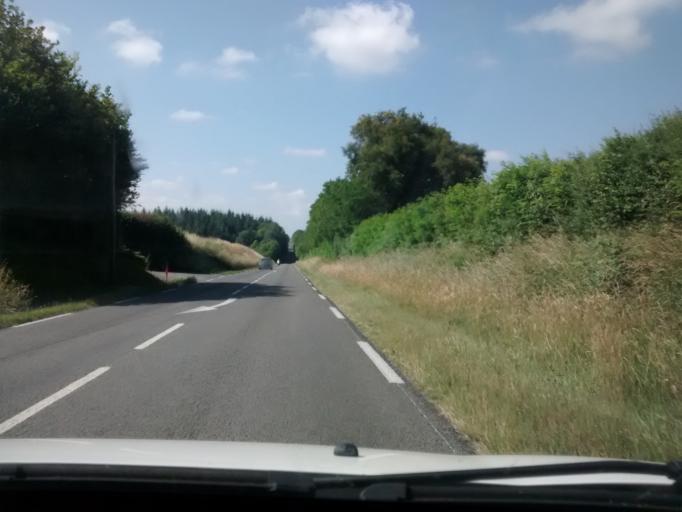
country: FR
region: Pays de la Loire
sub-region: Departement de la Sarthe
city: Saint-Calais
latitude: 47.9701
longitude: 0.7585
